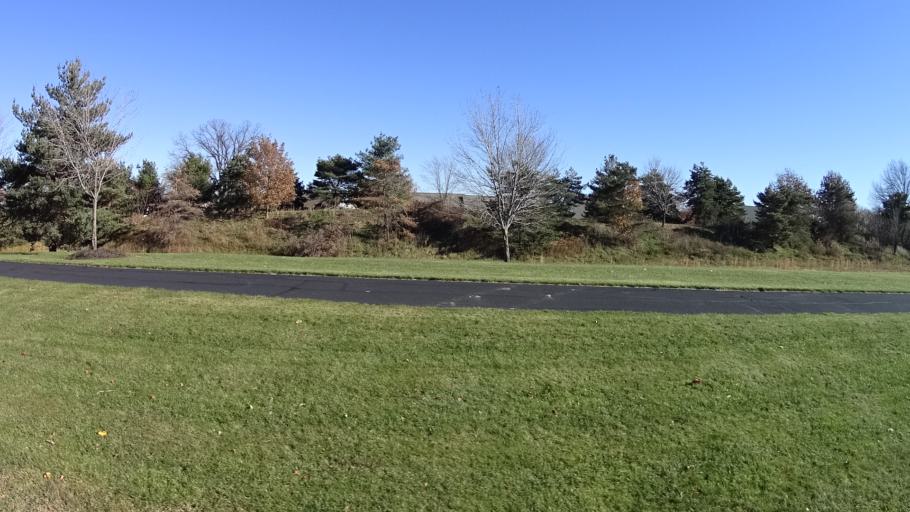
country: US
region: Ohio
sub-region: Lorain County
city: Avon Center
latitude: 41.4588
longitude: -82.0094
